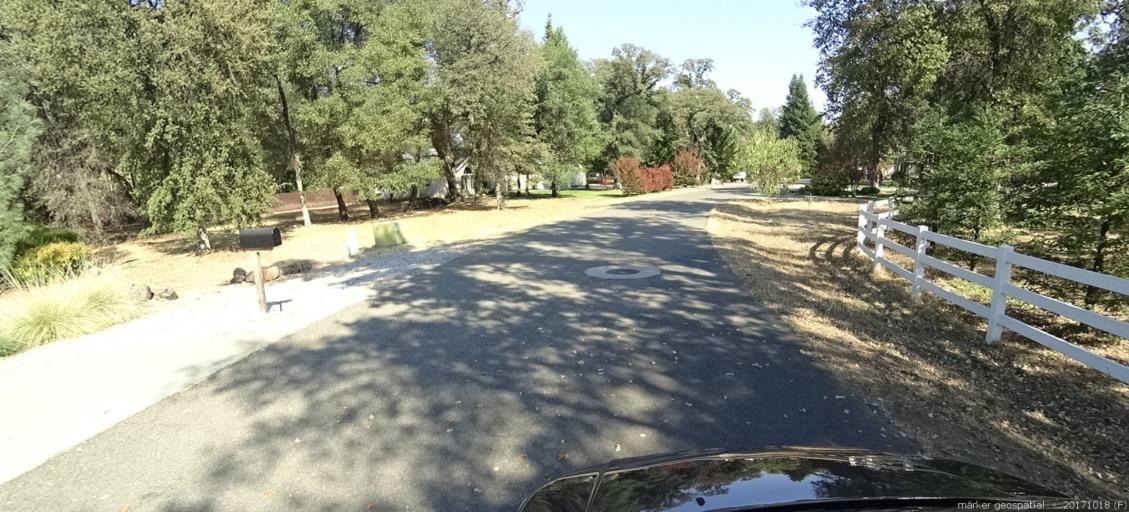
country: US
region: California
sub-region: Shasta County
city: Palo Cedro
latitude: 40.5661
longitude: -122.2362
